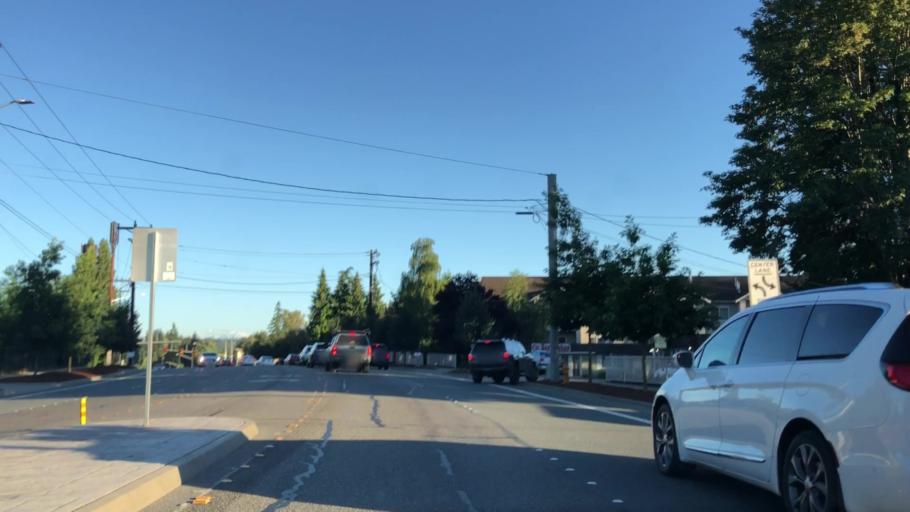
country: US
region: Washington
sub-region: King County
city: Bothell
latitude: 47.7819
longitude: -122.2206
